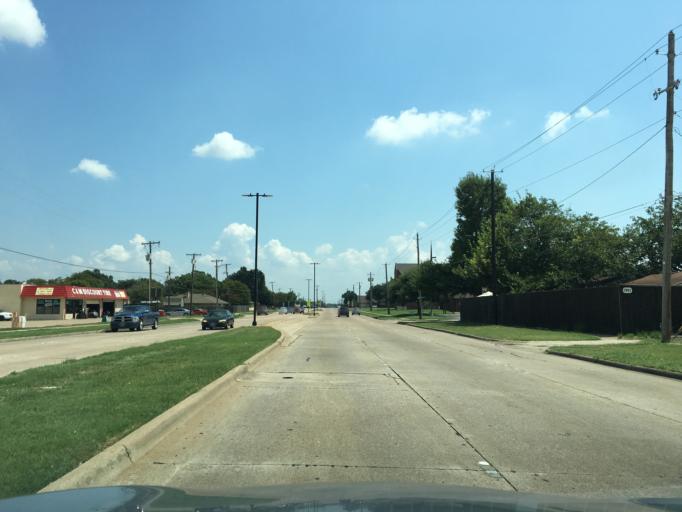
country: US
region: Texas
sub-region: Dallas County
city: Garland
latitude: 32.9311
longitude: -96.6473
